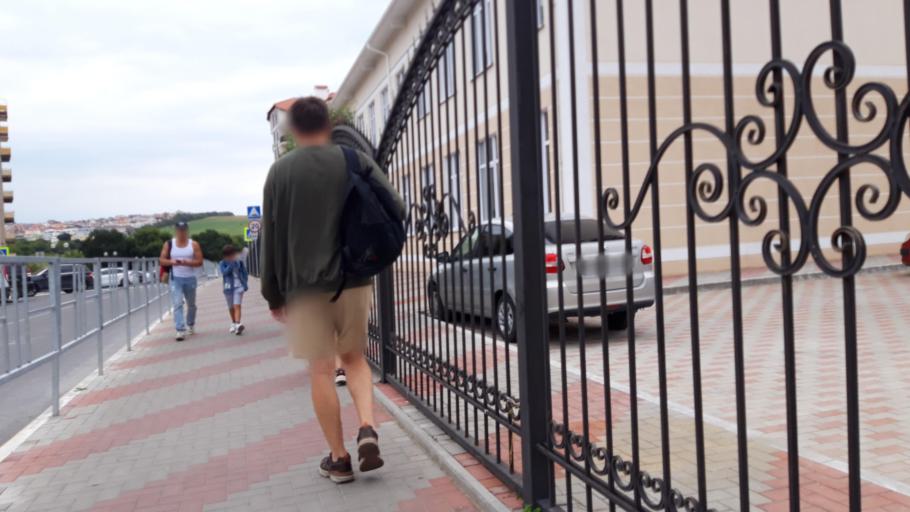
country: RU
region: Krasnodarskiy
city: Gelendzhik
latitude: 44.5512
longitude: 38.0598
